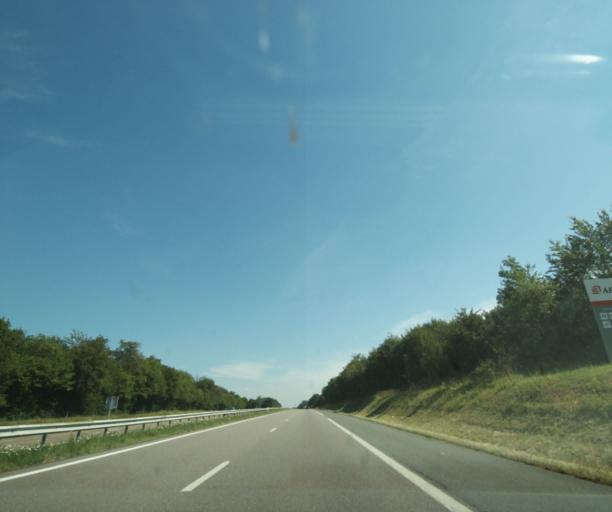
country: FR
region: Lorraine
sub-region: Departement de Meurthe-et-Moselle
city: Colombey-les-Belles
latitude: 48.5053
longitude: 5.9119
